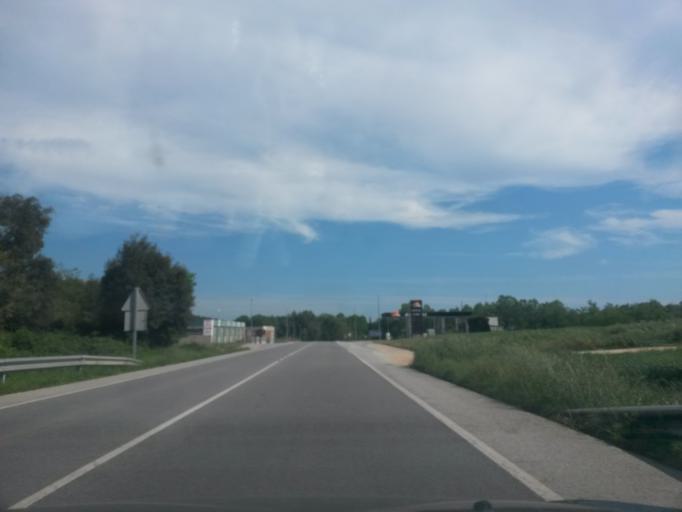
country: ES
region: Catalonia
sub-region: Provincia de Girona
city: Brunyola
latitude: 41.9085
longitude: 2.6602
